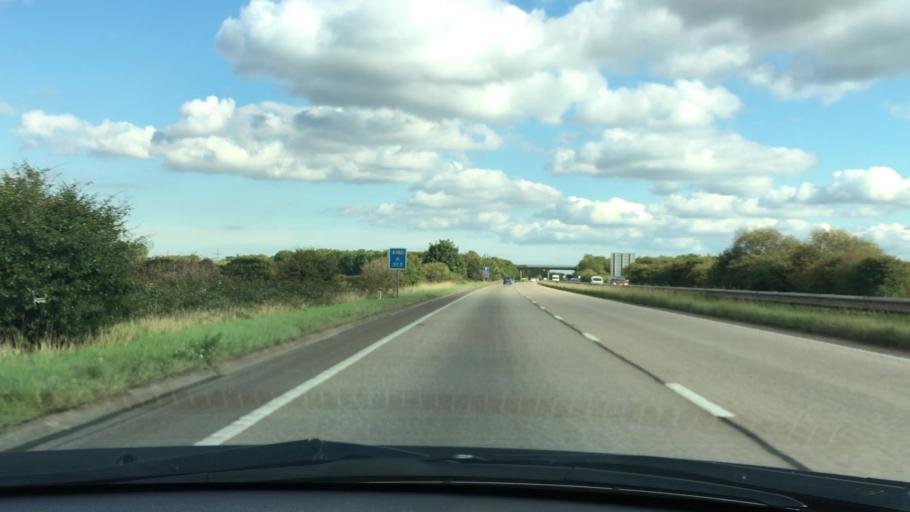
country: GB
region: England
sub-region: North East Lincolnshire
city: Healing
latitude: 53.5953
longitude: -0.1796
